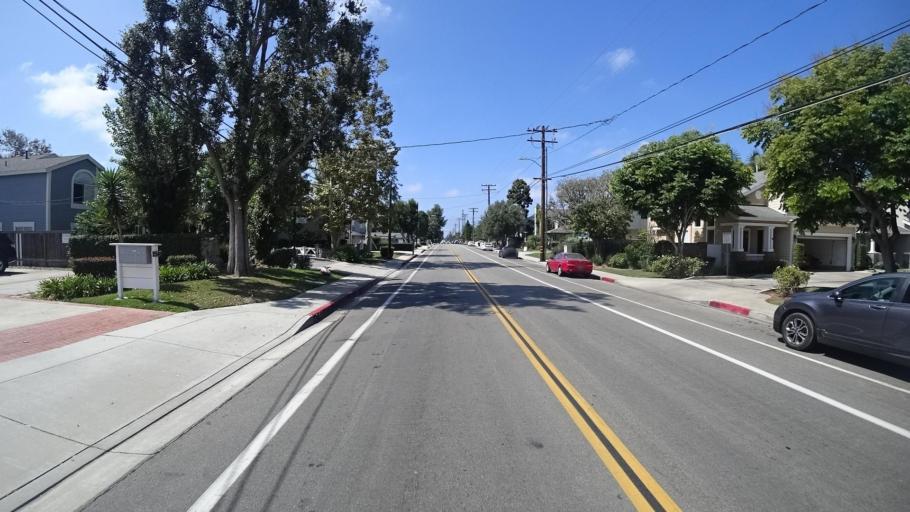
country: US
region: California
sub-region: Orange County
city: Costa Mesa
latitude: 33.6569
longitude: -117.8924
